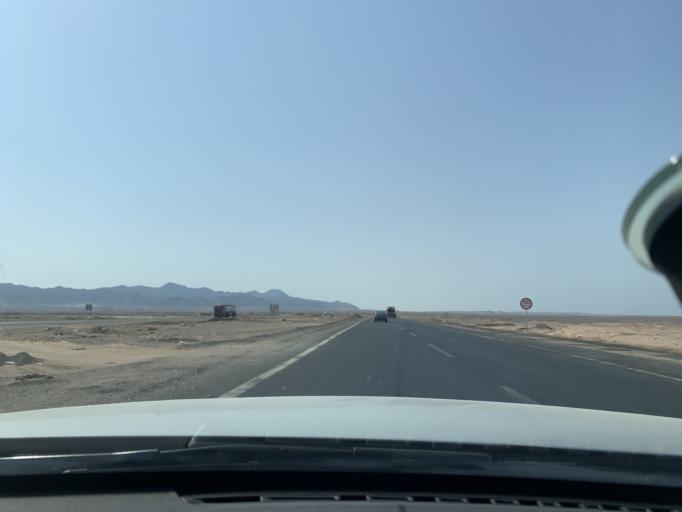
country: EG
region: Red Sea
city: El Gouna
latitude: 27.4340
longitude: 33.6076
